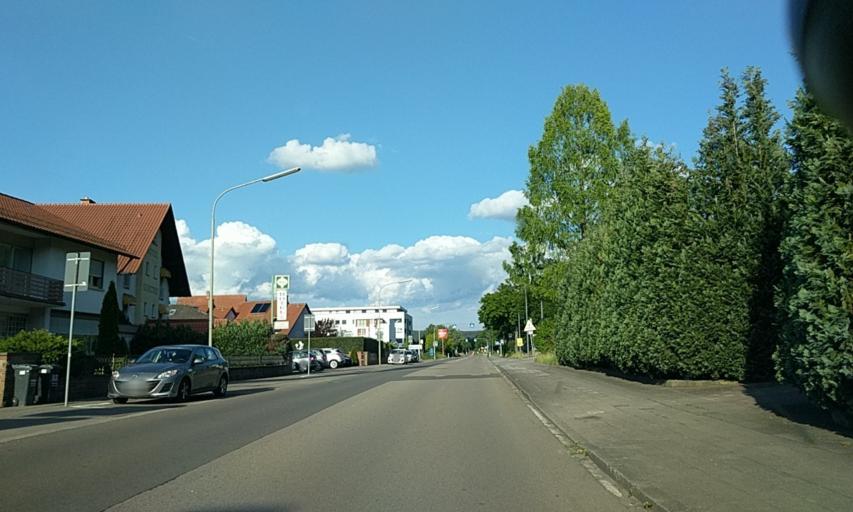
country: DE
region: Rheinland-Pfalz
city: Landstuhl
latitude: 49.4143
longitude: 7.5837
